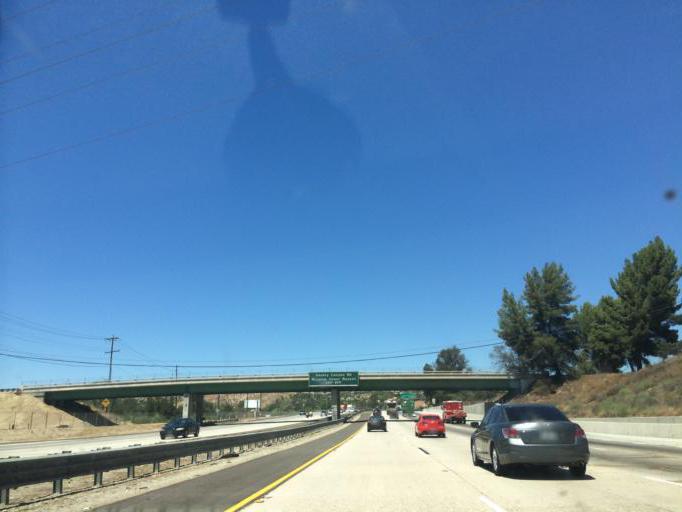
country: US
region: California
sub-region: Los Angeles County
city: Valencia
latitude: 34.4487
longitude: -118.6125
